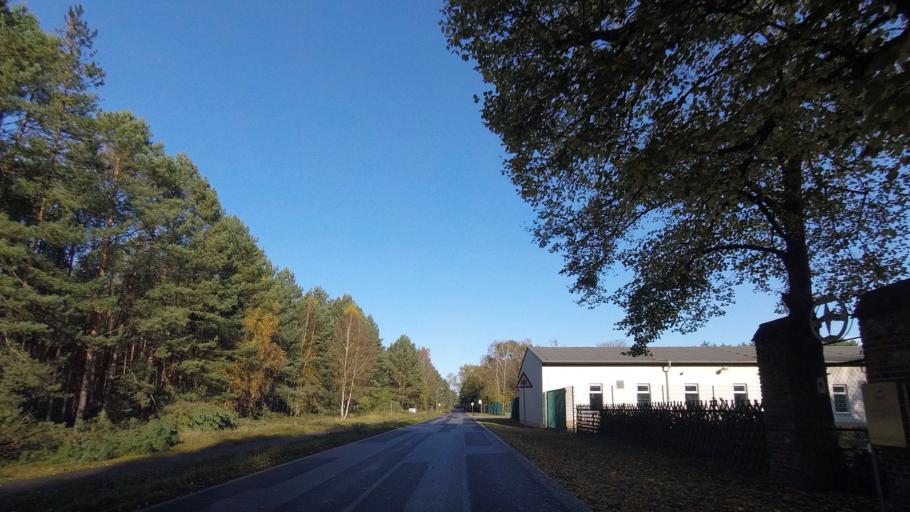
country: DE
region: Brandenburg
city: Borkwalde
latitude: 52.2395
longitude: 12.8524
